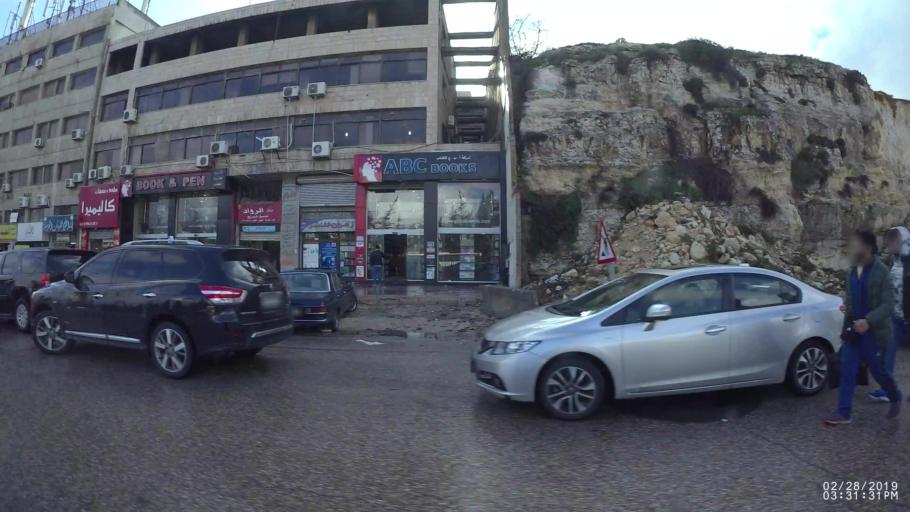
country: JO
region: Amman
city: Al Jubayhah
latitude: 32.0104
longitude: 35.8710
